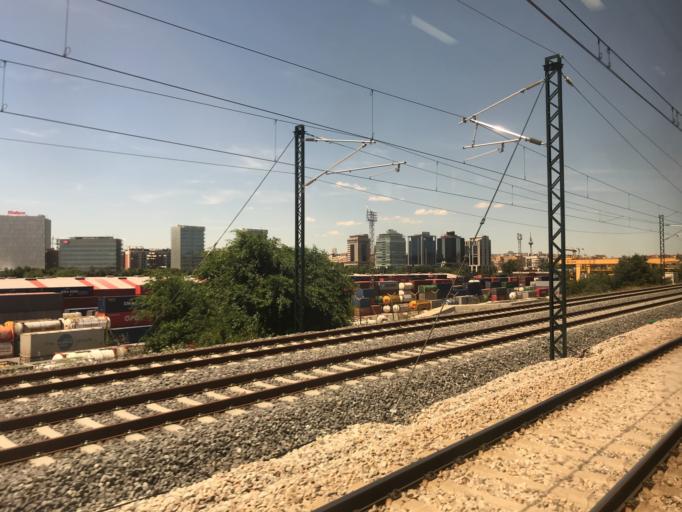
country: ES
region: Madrid
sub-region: Provincia de Madrid
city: Puente de Vallecas
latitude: 40.3865
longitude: -3.6768
